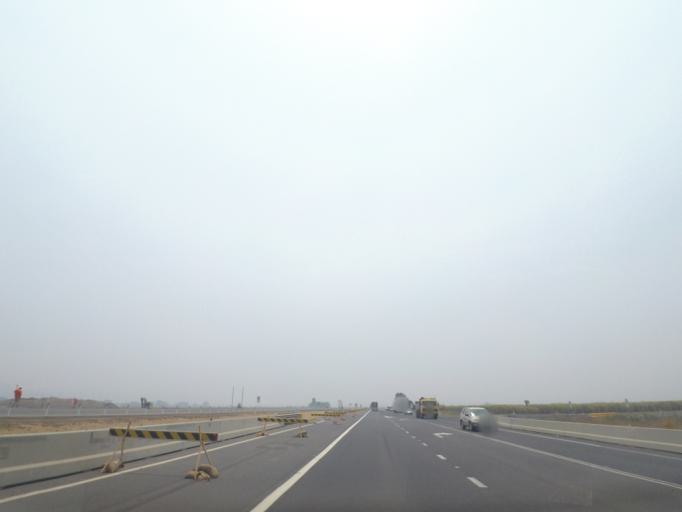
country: AU
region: New South Wales
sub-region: Clarence Valley
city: Maclean
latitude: -29.3933
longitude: 153.2395
